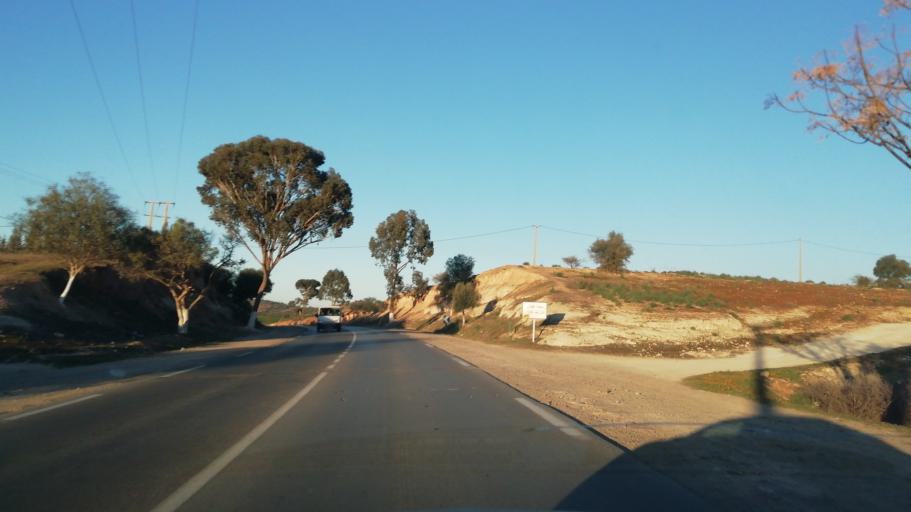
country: DZ
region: Tlemcen
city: Nedroma
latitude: 34.8562
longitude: -1.6796
